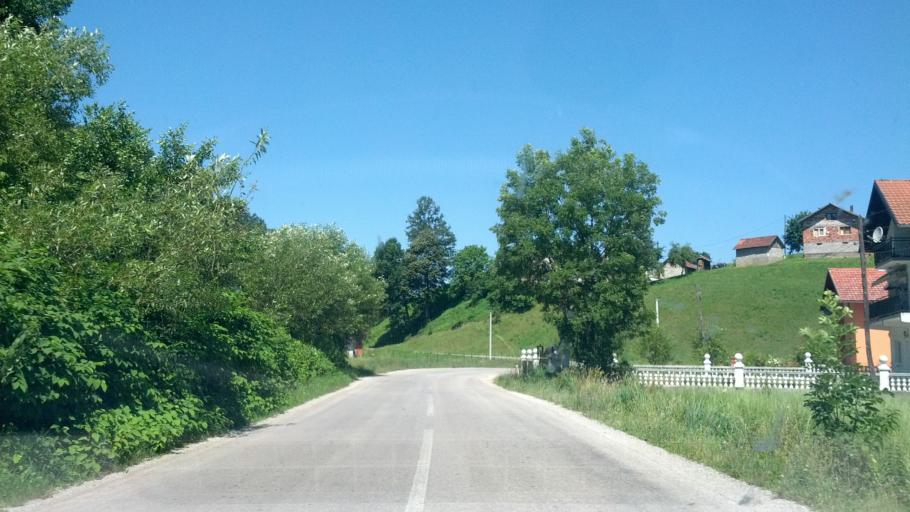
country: BA
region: Federation of Bosnia and Herzegovina
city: Otoka
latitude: 44.9923
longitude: 16.1617
